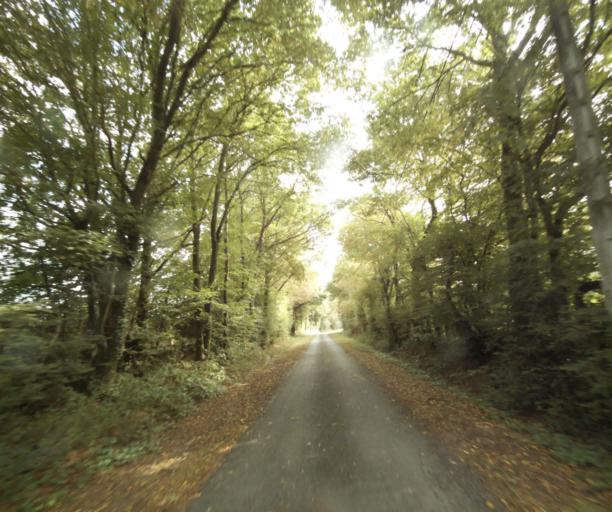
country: FR
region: Bourgogne
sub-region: Departement de Saone-et-Loire
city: Palinges
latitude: 46.5231
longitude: 4.2460
